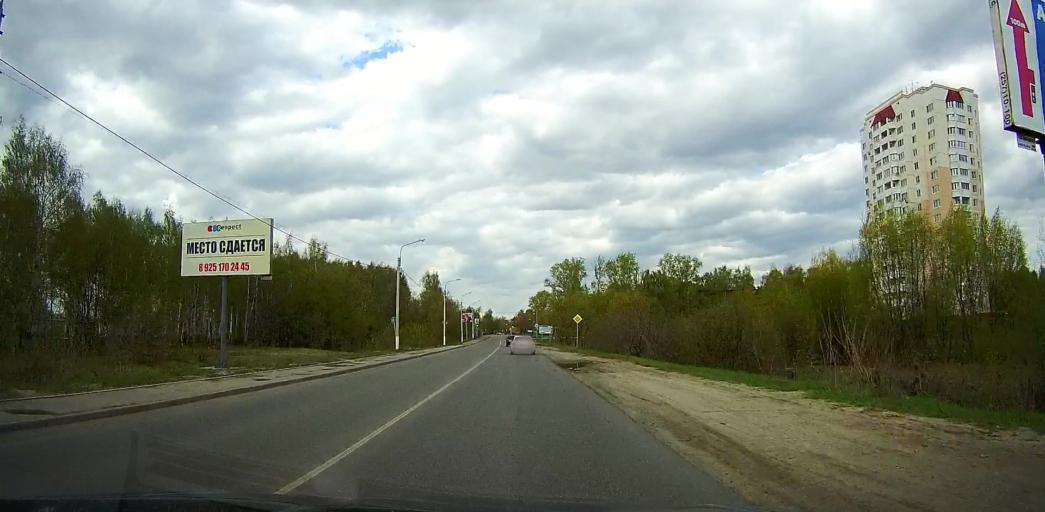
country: RU
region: Moskovskaya
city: Pavlovskiy Posad
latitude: 55.7640
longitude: 38.6567
